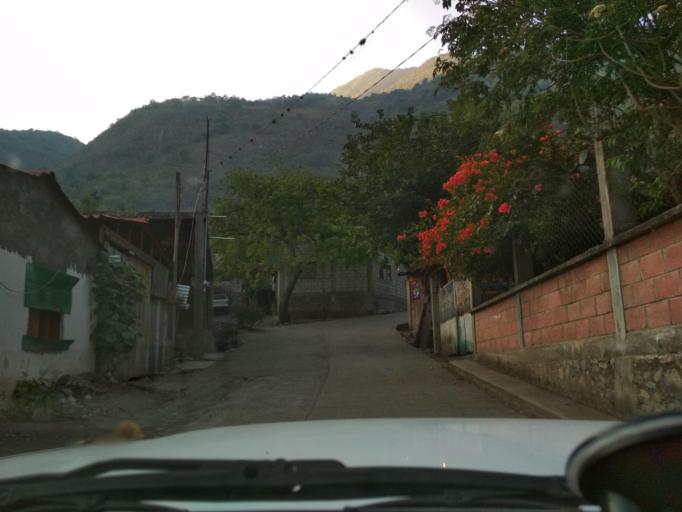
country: MX
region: Veracruz
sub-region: Nogales
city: Taza de Agua Ojo Zarco
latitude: 18.7714
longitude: -97.1947
